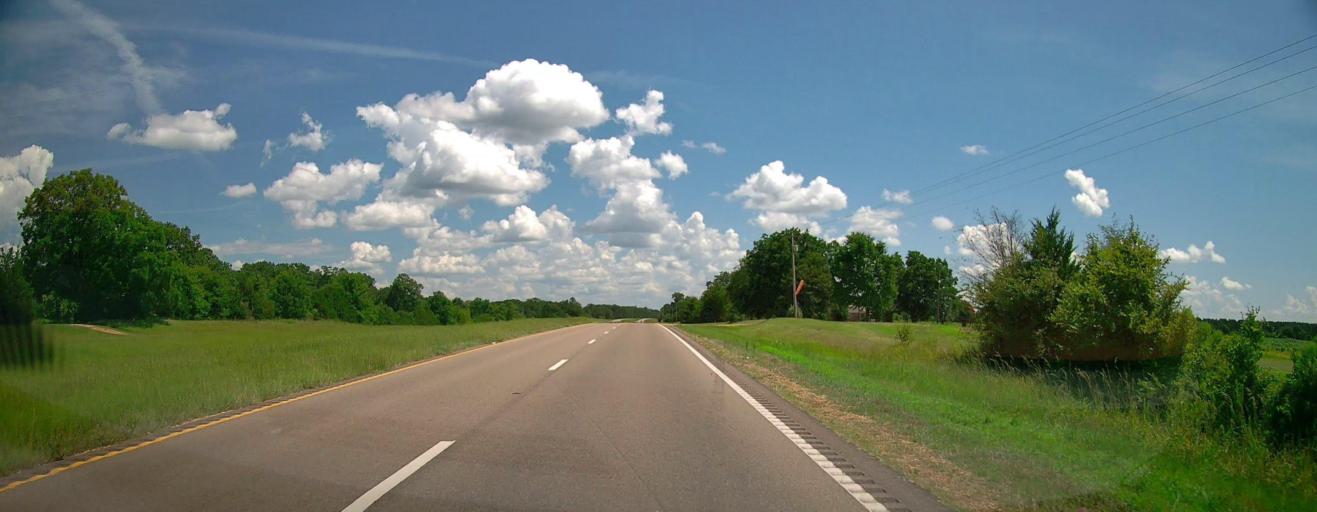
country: US
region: Mississippi
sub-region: Monroe County
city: Amory
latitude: 33.9500
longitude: -88.6030
